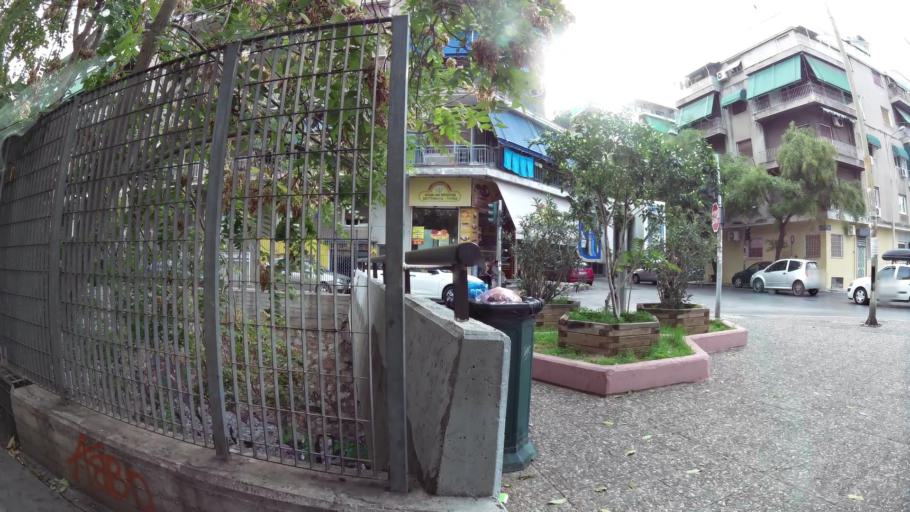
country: GR
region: Attica
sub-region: Nomarchia Athinas
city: Kipseli
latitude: 38.0014
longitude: 23.7233
